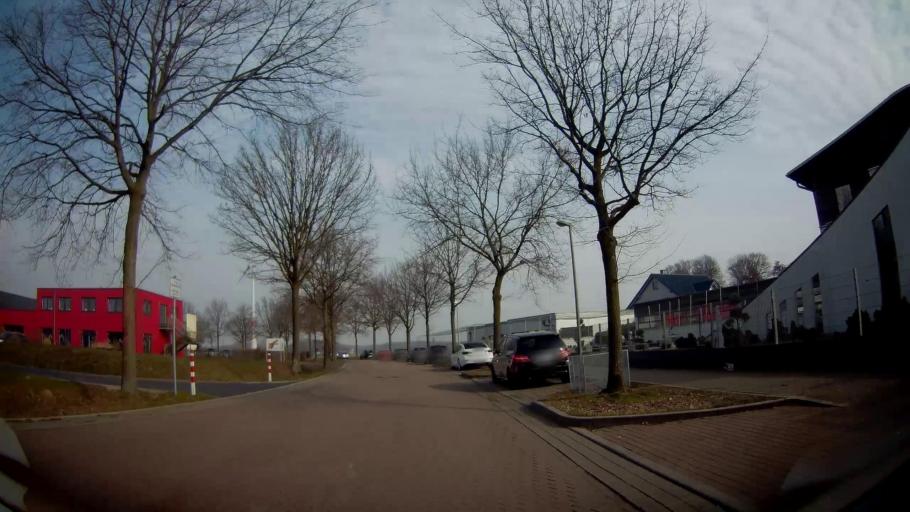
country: DE
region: North Rhine-Westphalia
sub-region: Regierungsbezirk Munster
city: Gladbeck
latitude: 51.5735
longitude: 6.9398
